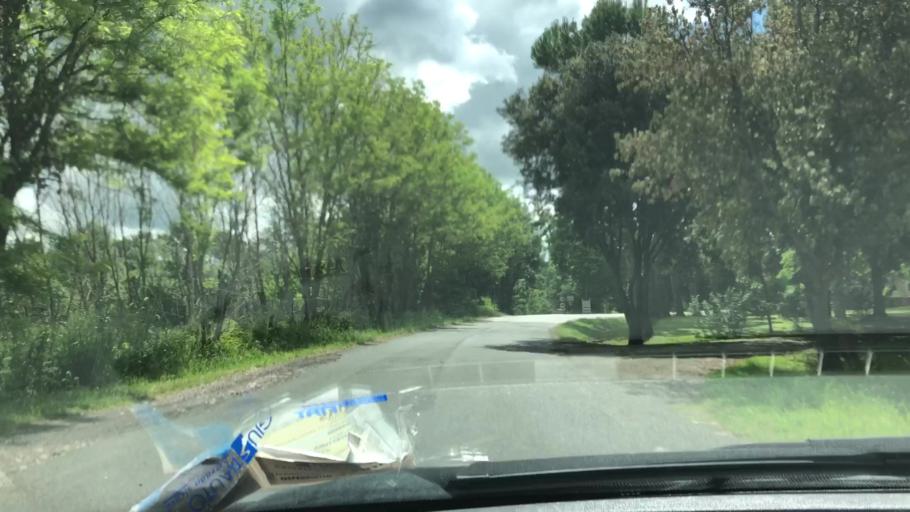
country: IT
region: Tuscany
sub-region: Province of Pisa
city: Saline
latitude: 43.3502
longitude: 10.7919
